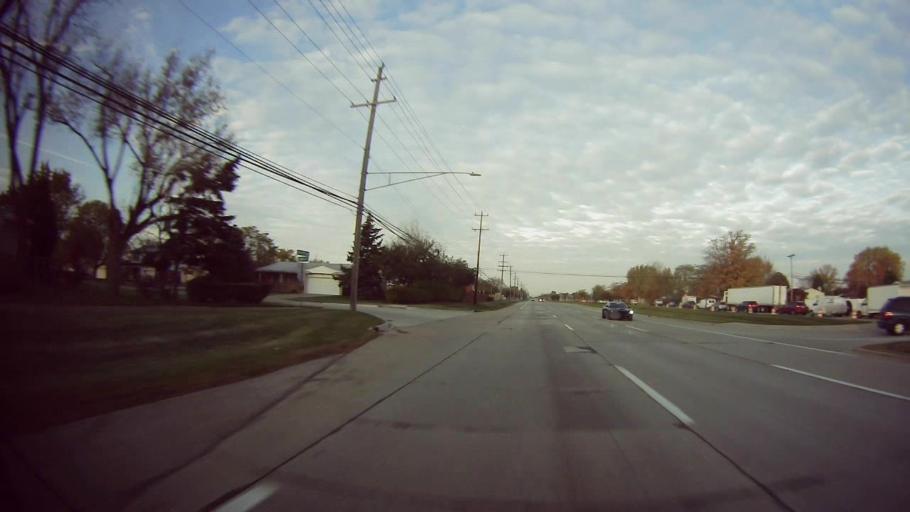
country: US
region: Michigan
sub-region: Macomb County
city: Sterling Heights
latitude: 42.5666
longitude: -83.0021
